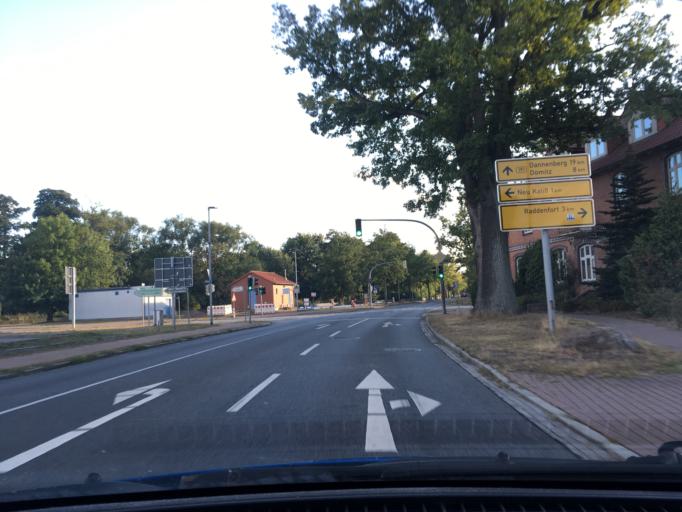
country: DE
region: Mecklenburg-Vorpommern
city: Neu Kaliss
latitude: 53.1783
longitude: 11.2911
